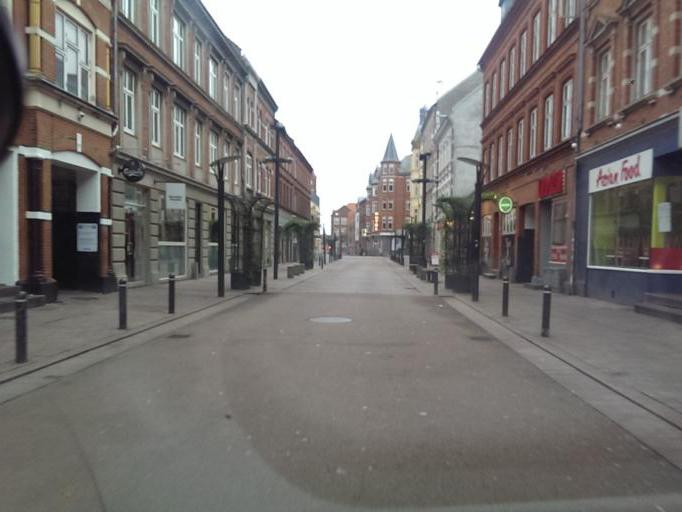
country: DK
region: South Denmark
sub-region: Esbjerg Kommune
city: Esbjerg
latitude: 55.4667
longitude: 8.4533
